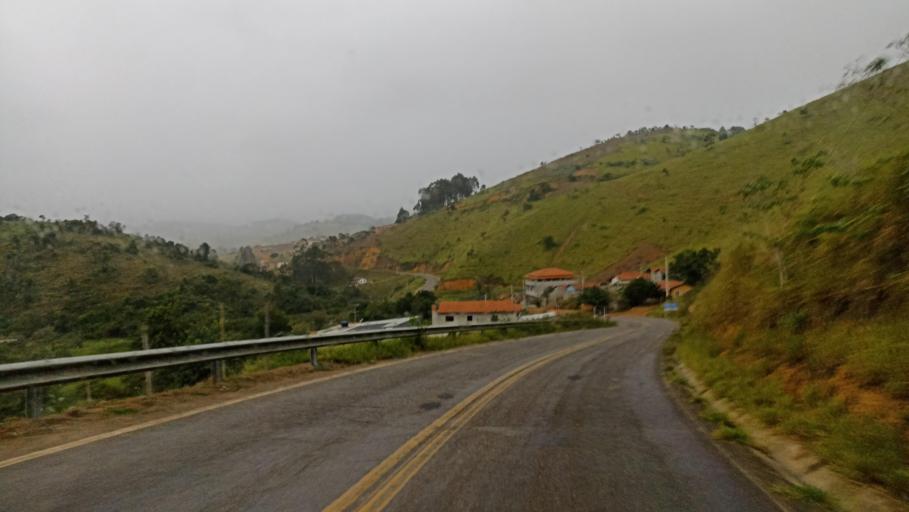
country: BR
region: Bahia
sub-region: Itanhem
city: Itanhem
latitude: -16.7345
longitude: -40.4342
